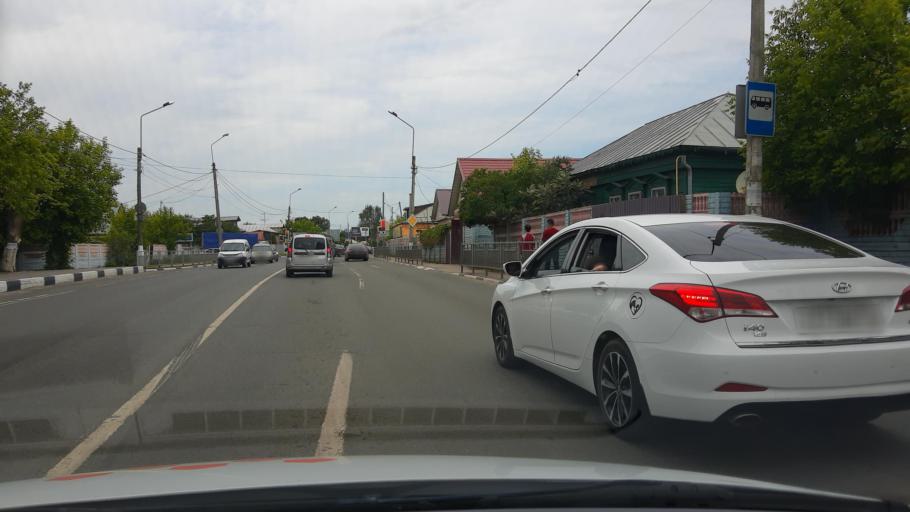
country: RU
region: Moskovskaya
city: Noginsk
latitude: 55.8688
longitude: 38.4384
